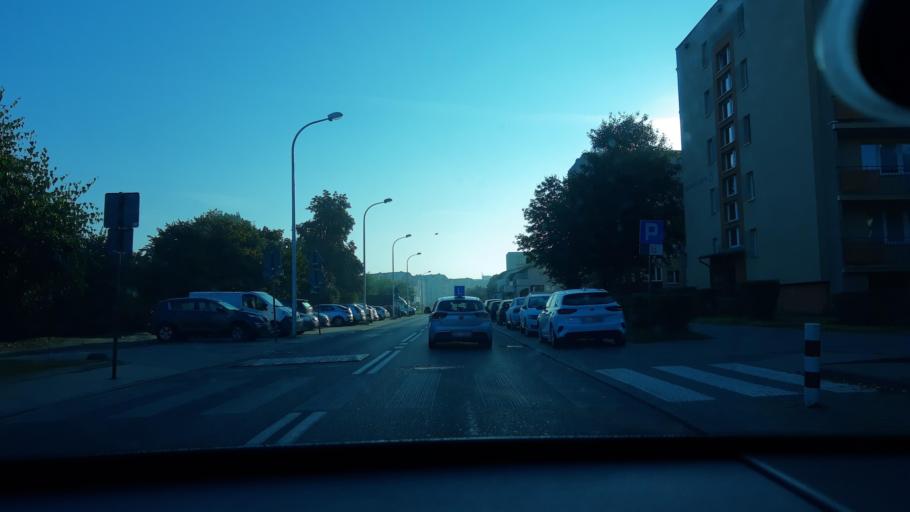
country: PL
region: Lodz Voivodeship
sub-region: Powiat sieradzki
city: Sieradz
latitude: 51.5938
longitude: 18.7206
